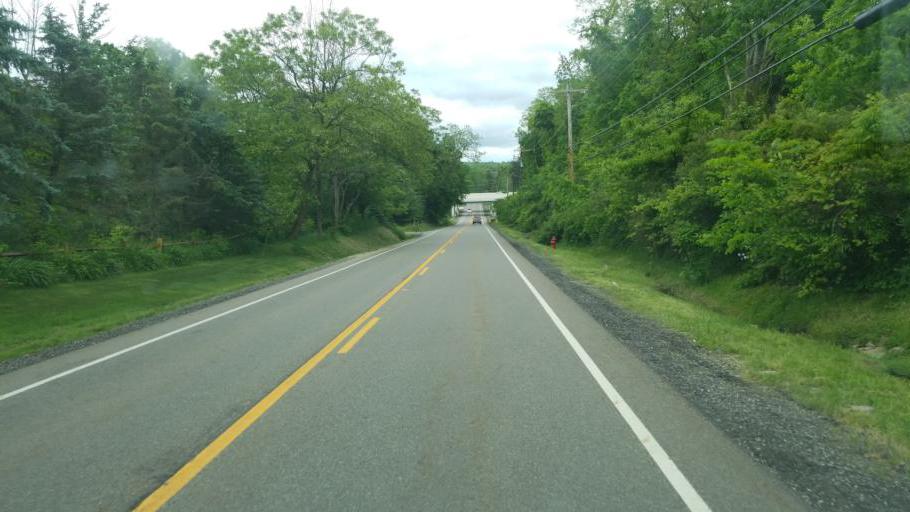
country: US
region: Ohio
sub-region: Summit County
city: Richfield
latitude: 41.2398
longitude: -81.6319
